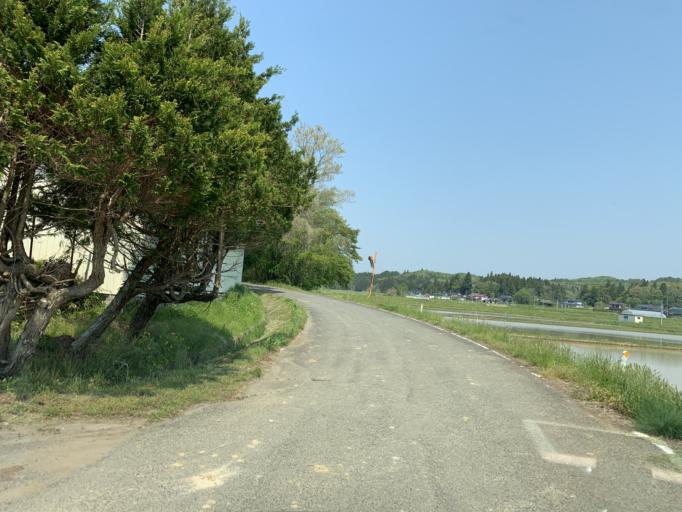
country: JP
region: Iwate
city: Ichinoseki
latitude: 38.8565
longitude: 141.0720
